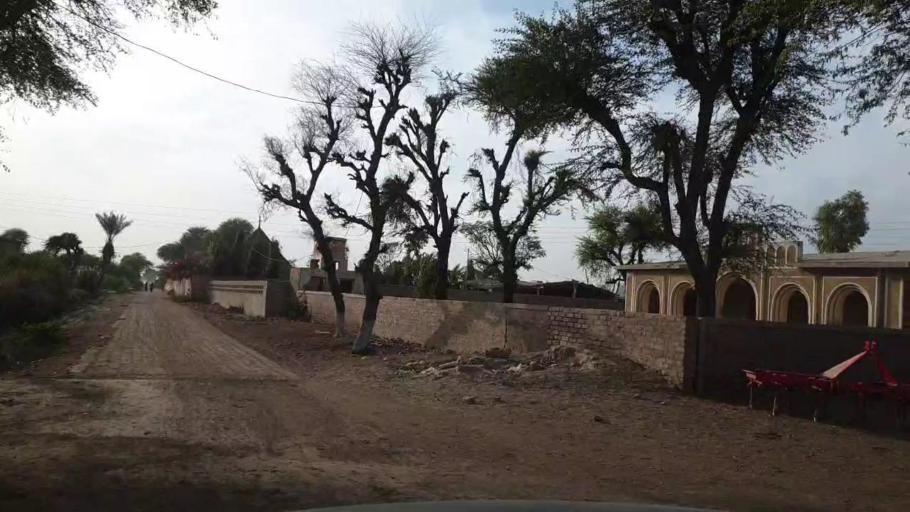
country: PK
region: Sindh
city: Kunri
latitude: 25.1951
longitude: 69.5199
